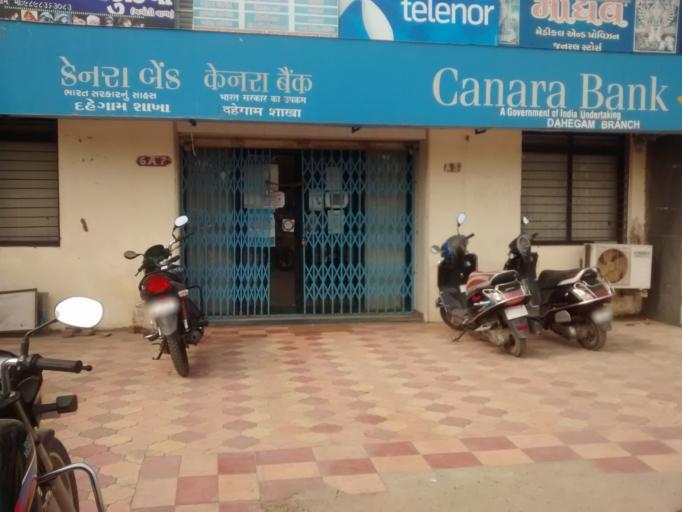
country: IN
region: Gujarat
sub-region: Gandhinagar
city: Dahegam
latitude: 23.1645
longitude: 72.8107
